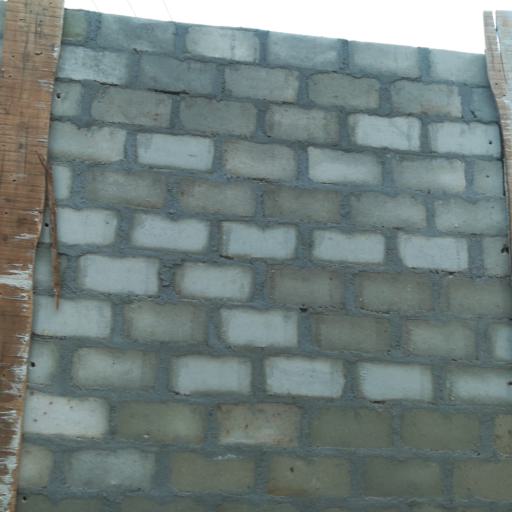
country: NG
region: Rivers
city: Port Harcourt
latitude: 4.7961
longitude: 7.0244
